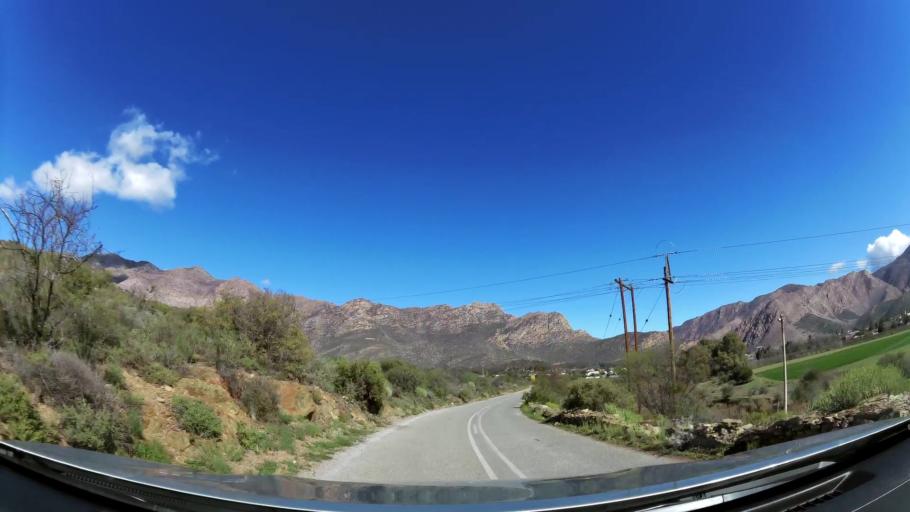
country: ZA
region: Western Cape
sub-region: Cape Winelands District Municipality
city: Ashton
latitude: -33.7897
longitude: 20.1321
